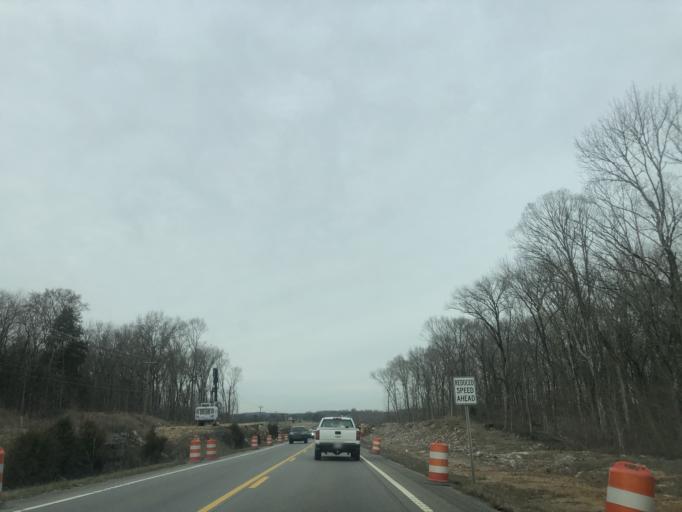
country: US
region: Tennessee
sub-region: Wilson County
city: Mount Juliet
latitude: 36.2744
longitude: -86.4420
